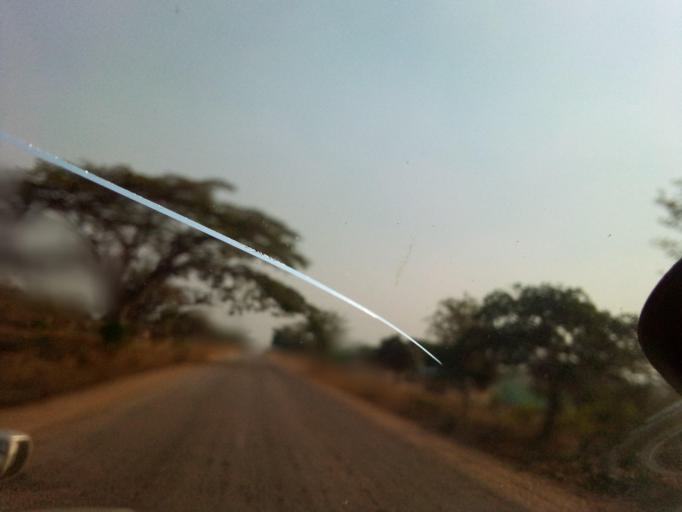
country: ZM
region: Northern
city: Chinsali
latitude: -10.9352
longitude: 32.0415
